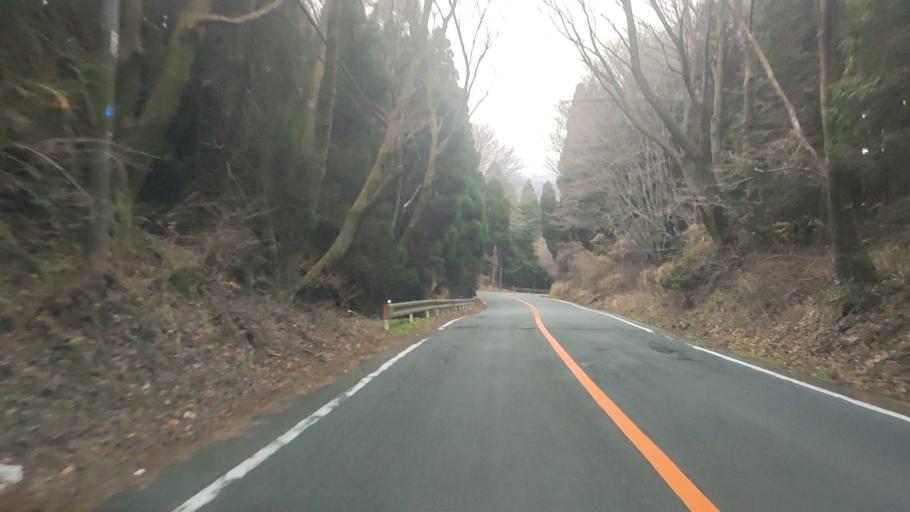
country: JP
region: Kumamoto
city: Aso
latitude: 32.8793
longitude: 131.1735
